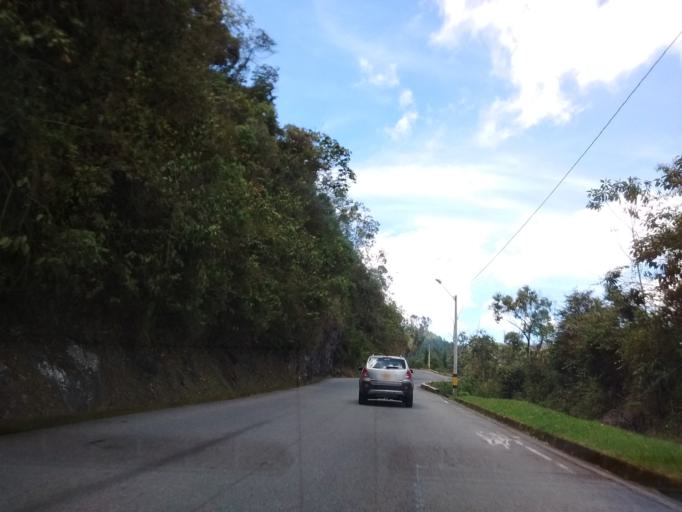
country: CO
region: Antioquia
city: Medellin
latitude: 6.2317
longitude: -75.5059
